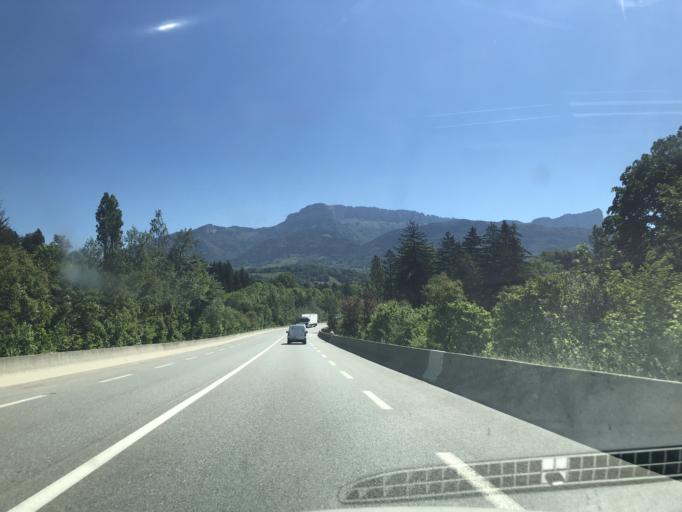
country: FR
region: Rhone-Alpes
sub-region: Departement de la Haute-Savoie
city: Annecy-le-Vieux
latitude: 45.9378
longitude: 6.1450
